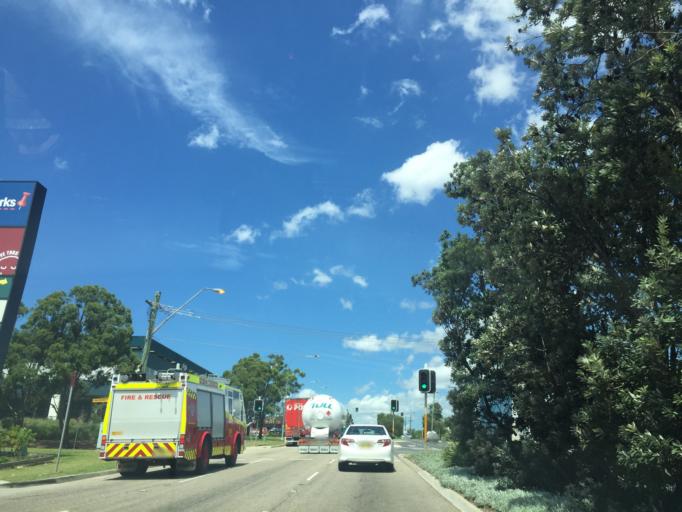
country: AU
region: New South Wales
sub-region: Strathfield
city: Strathfield South
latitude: -33.9002
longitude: 151.0652
